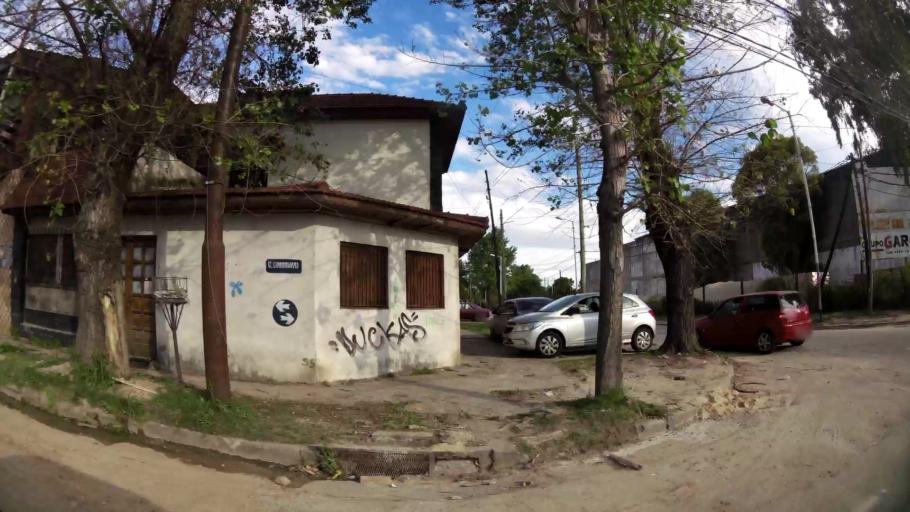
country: AR
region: Buenos Aires
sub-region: Partido de Lanus
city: Lanus
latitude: -34.7097
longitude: -58.3481
